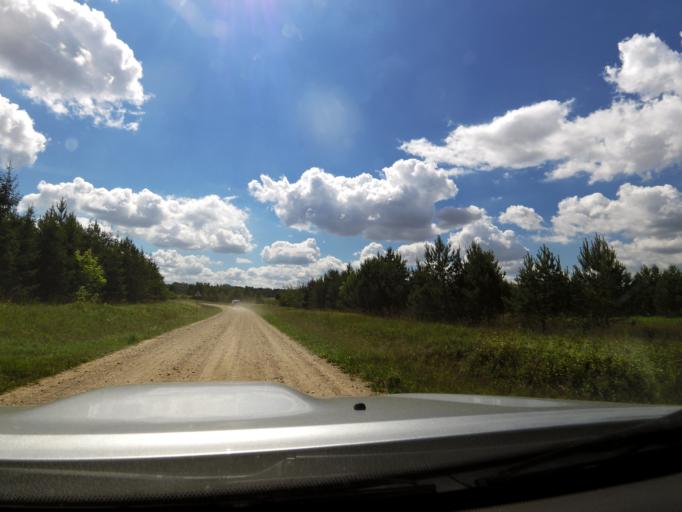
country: LT
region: Vilnius County
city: Elektrenai
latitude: 54.9470
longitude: 24.6737
